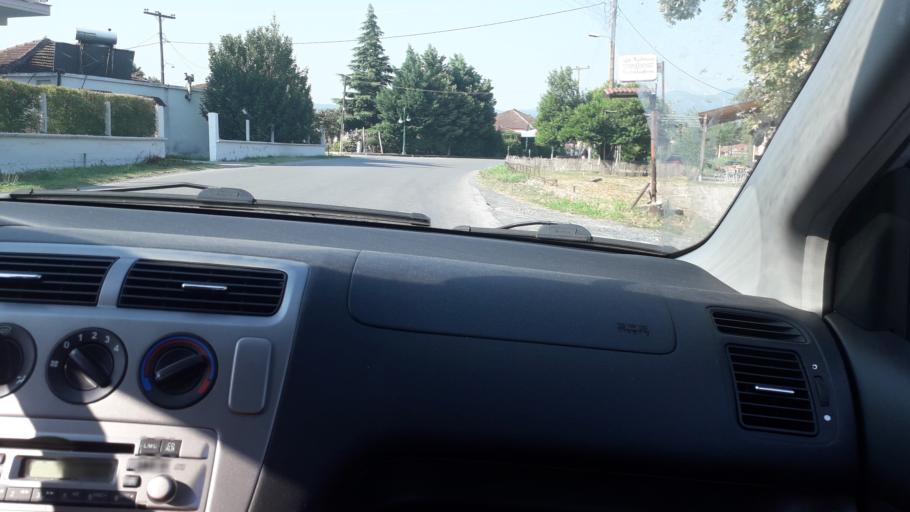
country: GR
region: Central Macedonia
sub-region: Nomos Pellis
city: Tsakoi
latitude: 40.9565
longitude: 22.0446
